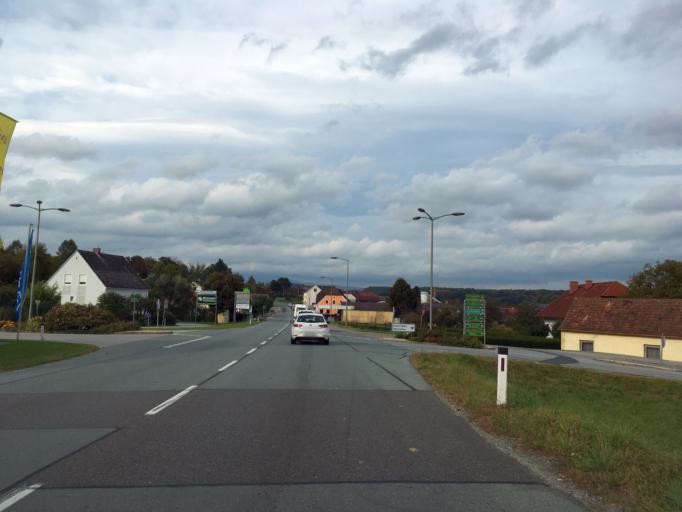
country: AT
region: Styria
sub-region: Politischer Bezirk Hartberg-Fuerstenfeld
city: Grafendorf bei Hartberg
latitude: 47.3282
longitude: 15.9911
